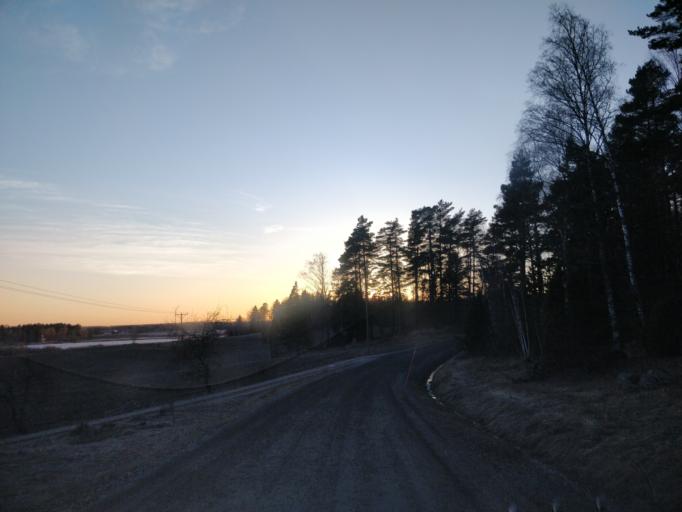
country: SE
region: Uppsala
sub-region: Enkopings Kommun
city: Orsundsbro
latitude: 59.8247
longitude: 17.1531
